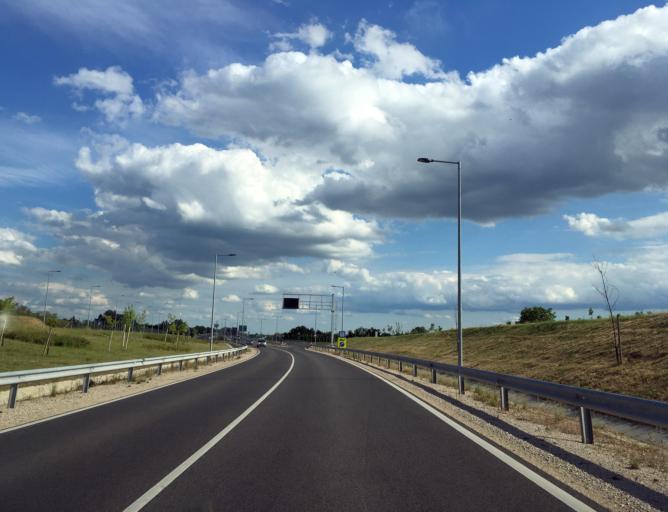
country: HU
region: Komarom-Esztergom
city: Komarom
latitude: 47.7523
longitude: 18.0851
